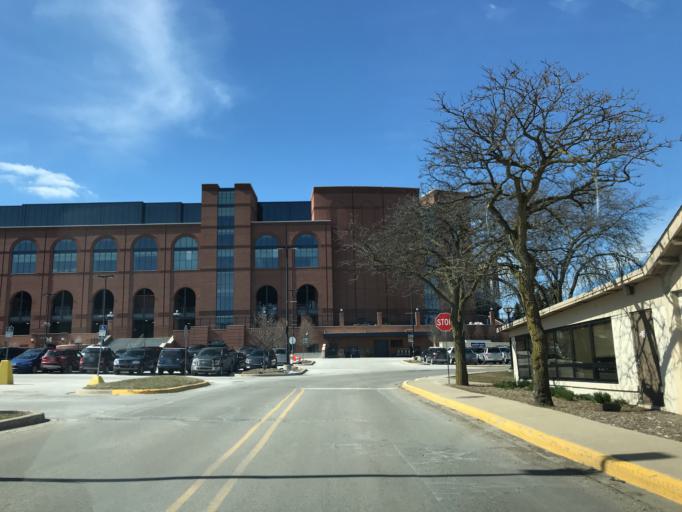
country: US
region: Michigan
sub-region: Washtenaw County
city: Ann Arbor
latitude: 42.2663
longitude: -83.7457
